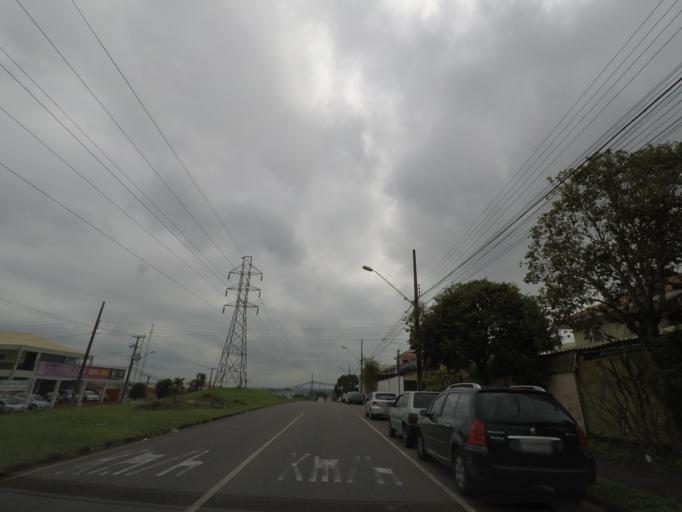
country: BR
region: Parana
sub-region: Curitiba
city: Curitiba
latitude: -25.5032
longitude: -49.3149
